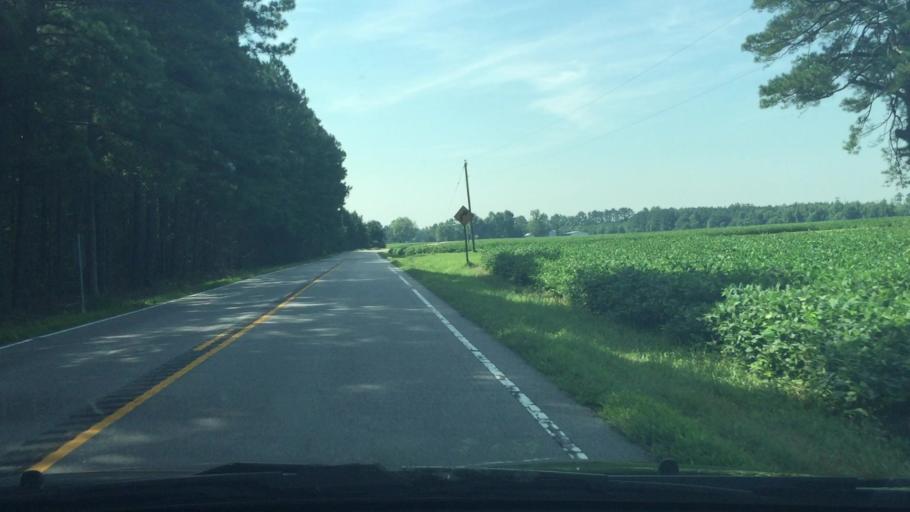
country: US
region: Virginia
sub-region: Southampton County
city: Courtland
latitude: 36.8486
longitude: -77.1332
